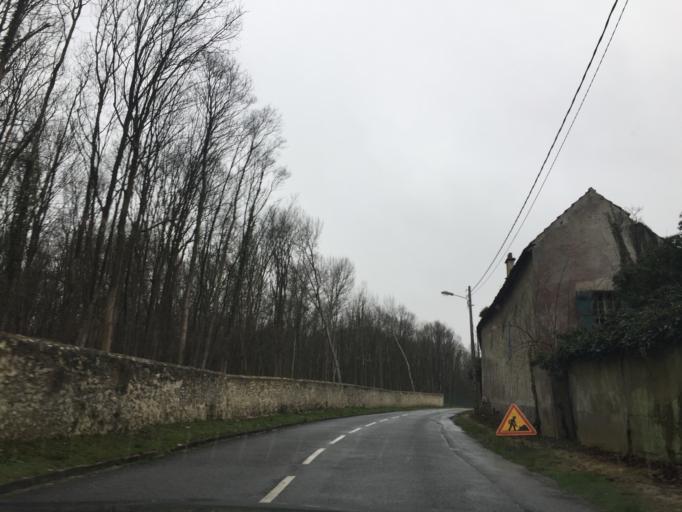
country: FR
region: Ile-de-France
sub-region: Departement de Seine-et-Marne
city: Coupvray
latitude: 48.8866
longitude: 2.7929
